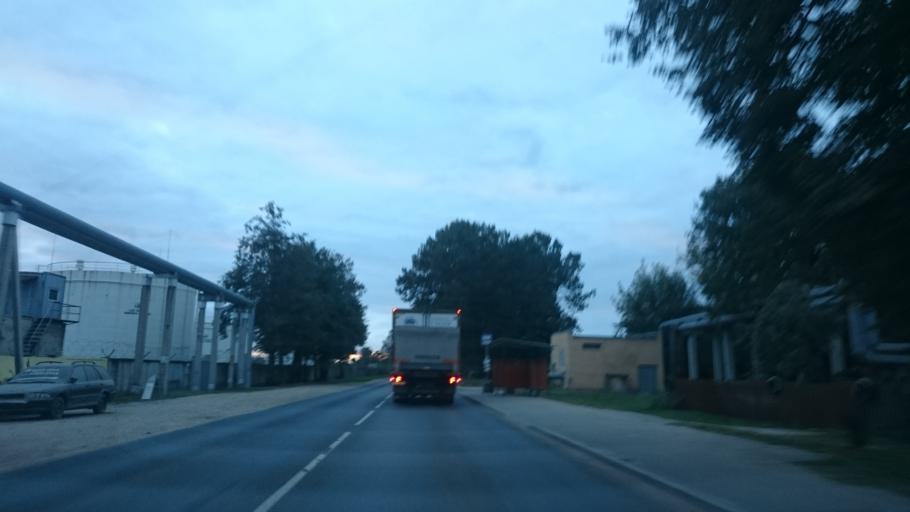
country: LV
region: Kekava
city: Kekava
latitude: 56.9121
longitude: 24.2053
